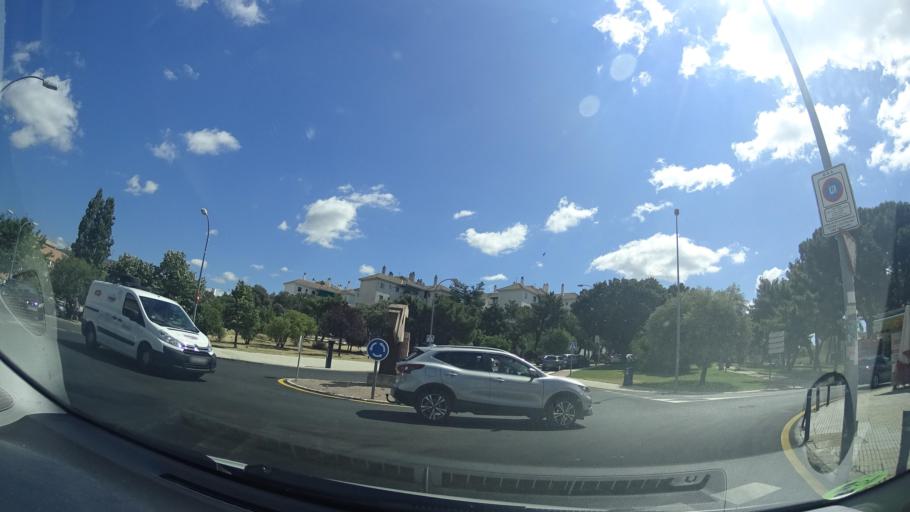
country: ES
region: Madrid
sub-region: Provincia de Madrid
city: Collado-Villalba
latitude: 40.6269
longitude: -4.0026
